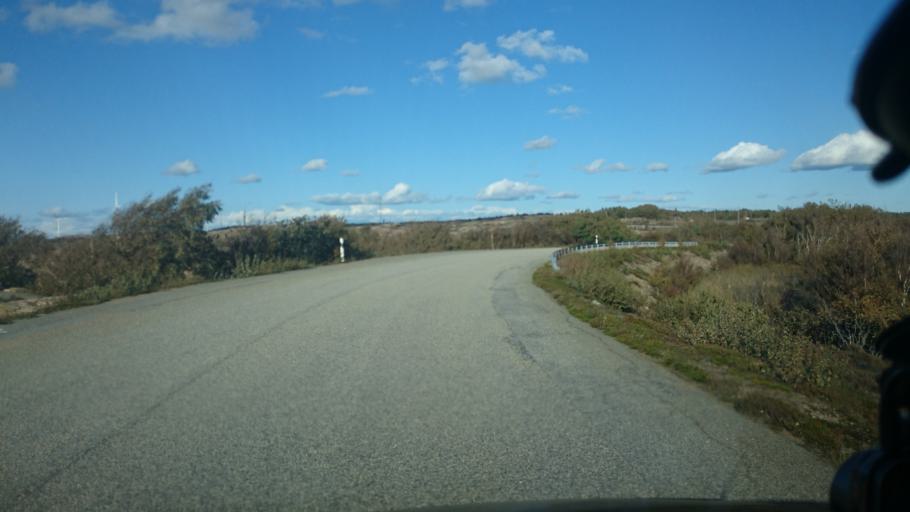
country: SE
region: Vaestra Goetaland
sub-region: Lysekils Kommun
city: Lysekil
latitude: 58.3188
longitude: 11.4096
